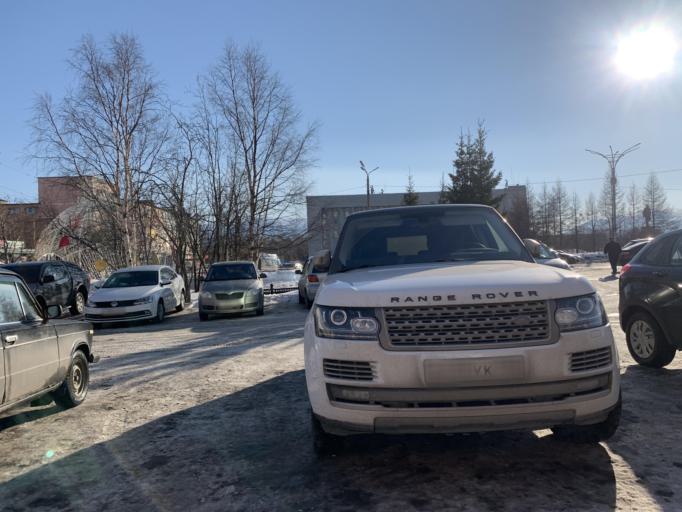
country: RU
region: Murmansk
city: Monchegorsk
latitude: 67.9396
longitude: 32.9389
